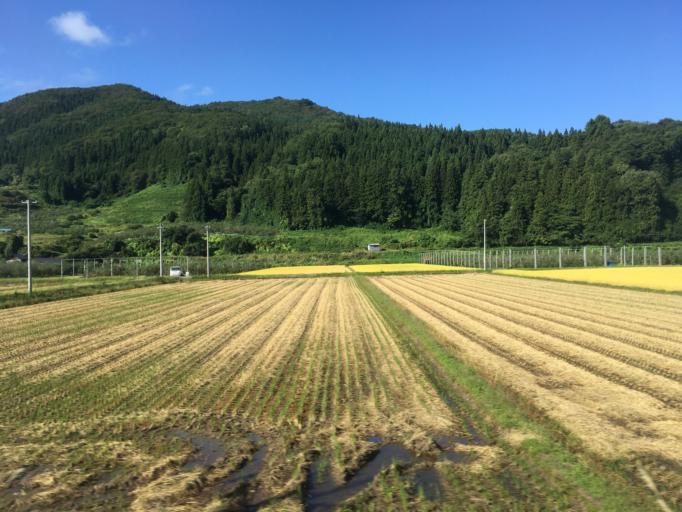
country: JP
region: Aomori
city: Hirosaki
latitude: 40.5328
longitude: 140.5477
